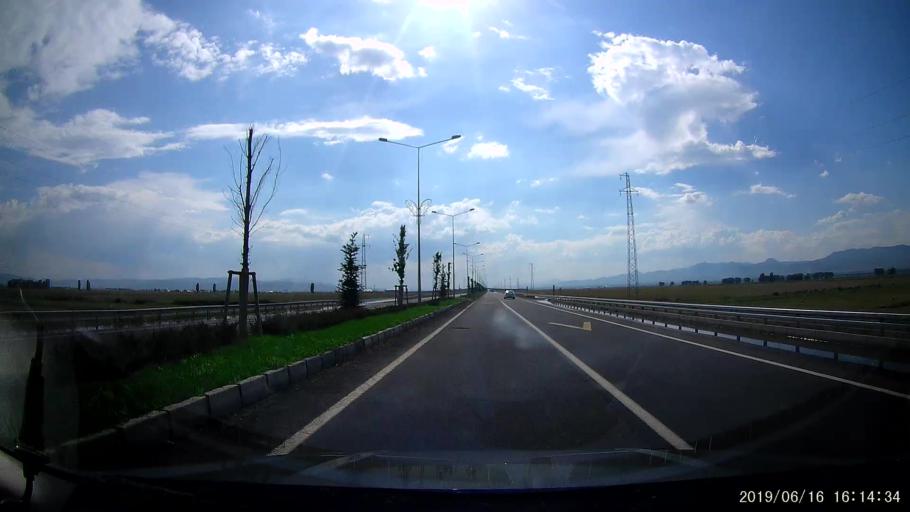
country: TR
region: Erzurum
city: Erzurum
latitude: 39.9609
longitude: 41.2458
